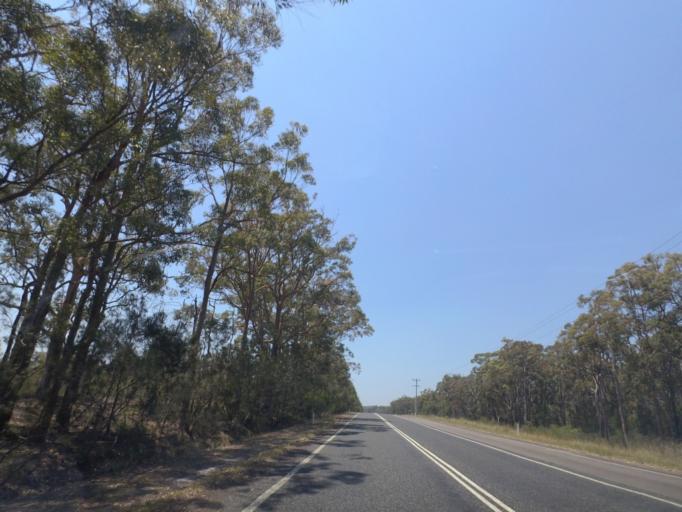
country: AU
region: New South Wales
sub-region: Port Stephens Shire
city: Port Stephens
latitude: -32.6388
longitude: 152.0261
